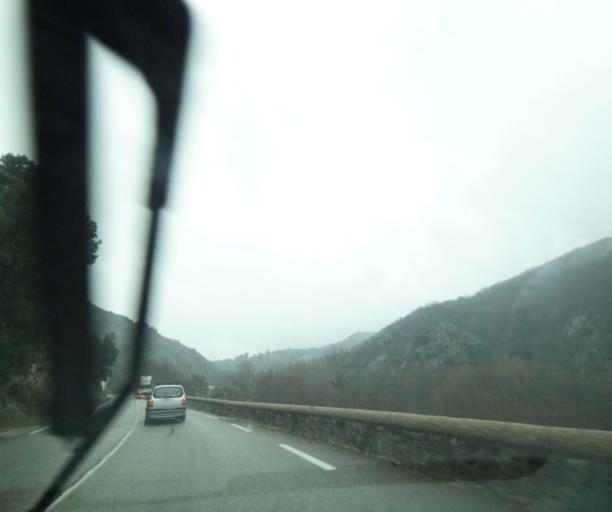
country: FR
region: Rhone-Alpes
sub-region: Departement de l'Ardeche
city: Thueyts
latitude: 44.6759
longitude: 4.2427
